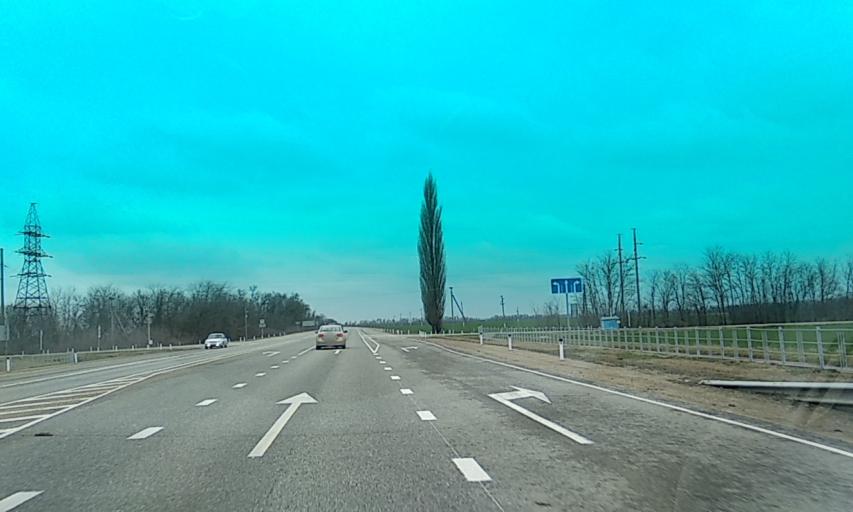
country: RU
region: Adygeya
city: Krasnogvardeyskoye
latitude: 45.1302
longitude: 39.6357
